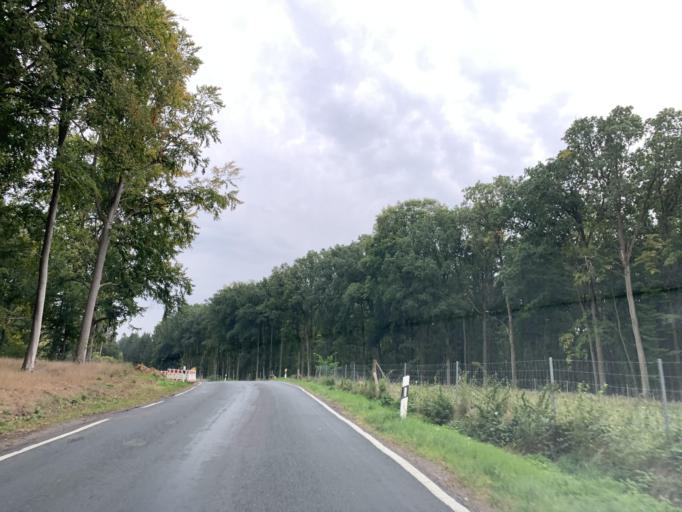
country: DE
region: Mecklenburg-Vorpommern
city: Woldegk
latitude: 53.3345
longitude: 13.6587
